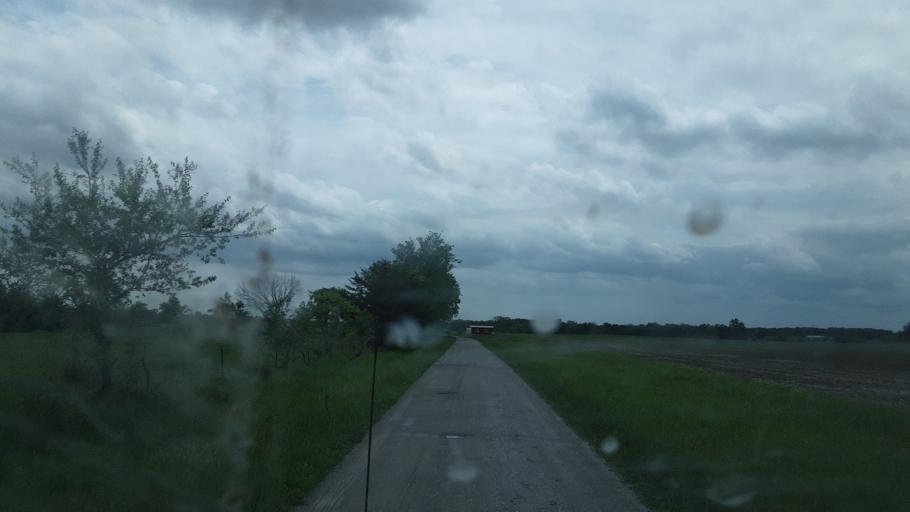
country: US
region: Missouri
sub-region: Clark County
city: Kahoka
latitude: 40.4399
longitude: -91.6056
